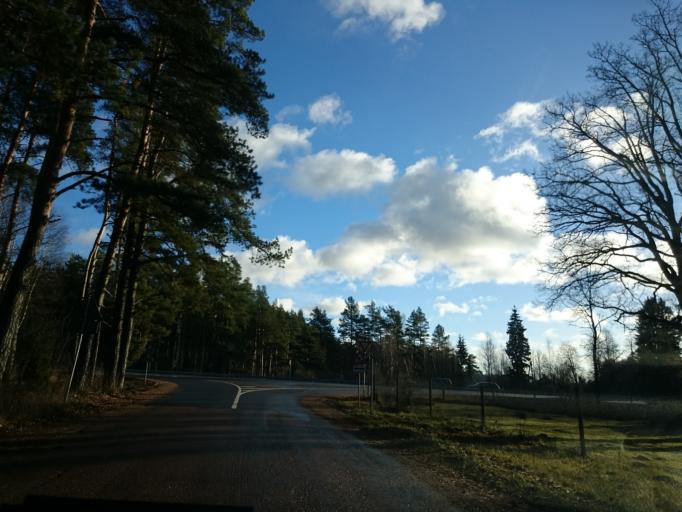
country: LV
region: Garkalne
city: Garkalne
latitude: 57.0480
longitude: 24.4383
